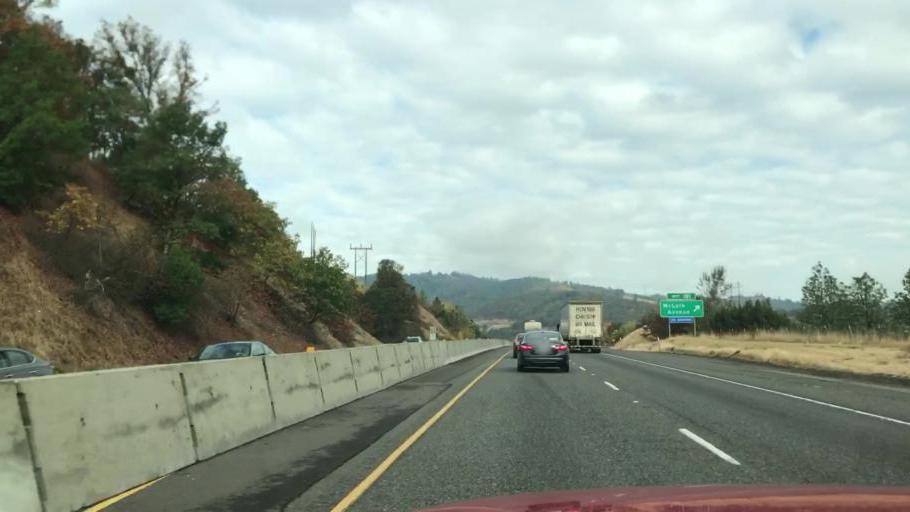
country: US
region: Oregon
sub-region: Douglas County
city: Green
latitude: 43.1740
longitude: -123.3699
